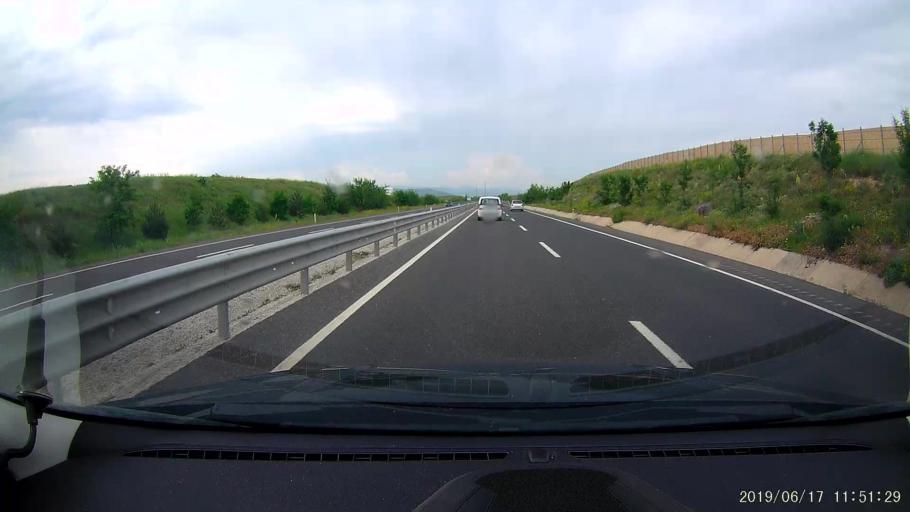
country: TR
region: Cankiri
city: Atkaracalar
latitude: 40.8175
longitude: 33.1054
